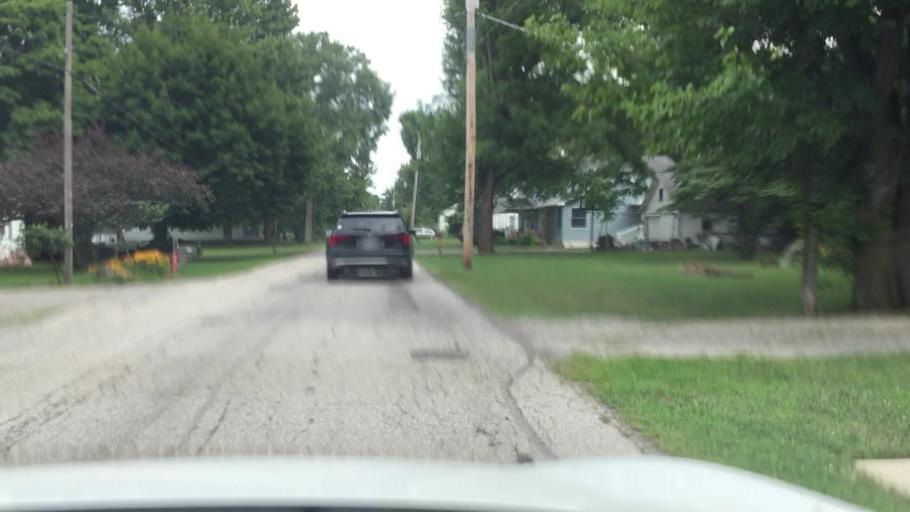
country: US
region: Ohio
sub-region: Union County
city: Marysville
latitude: 40.1829
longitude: -83.4376
